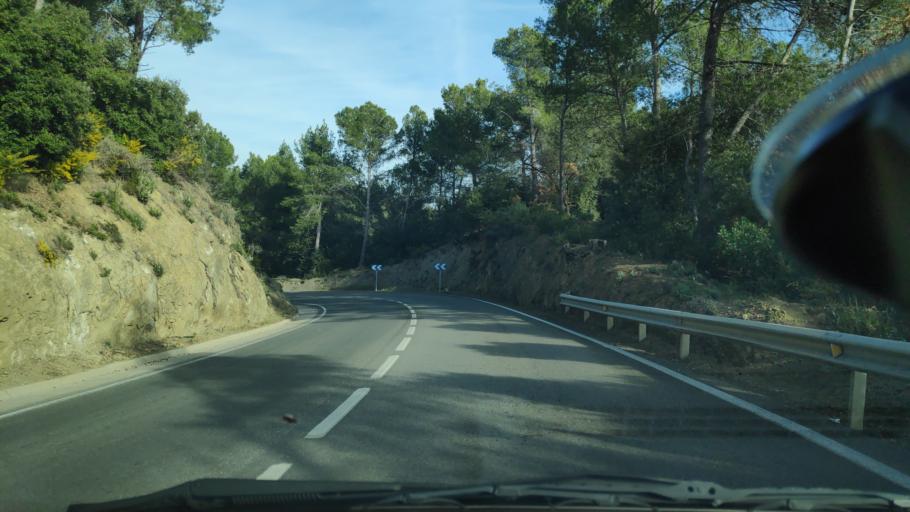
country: ES
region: Catalonia
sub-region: Provincia de Barcelona
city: Matadepera
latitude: 41.5979
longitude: 2.0502
